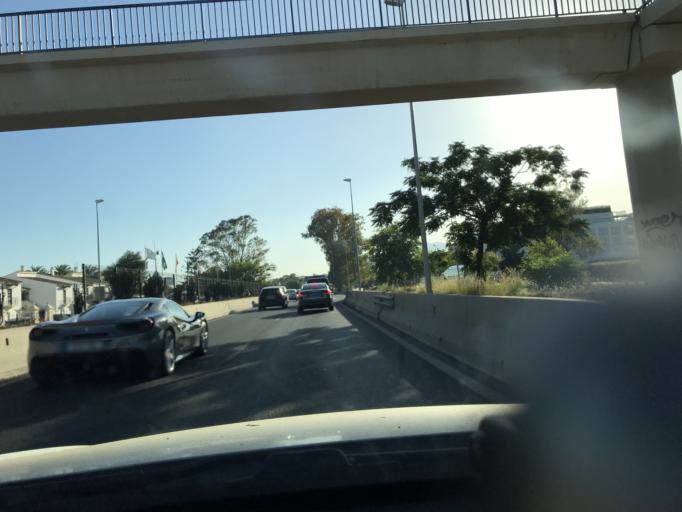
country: ES
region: Andalusia
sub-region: Provincia de Malaga
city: Benahavis
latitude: 36.4870
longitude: -4.9686
